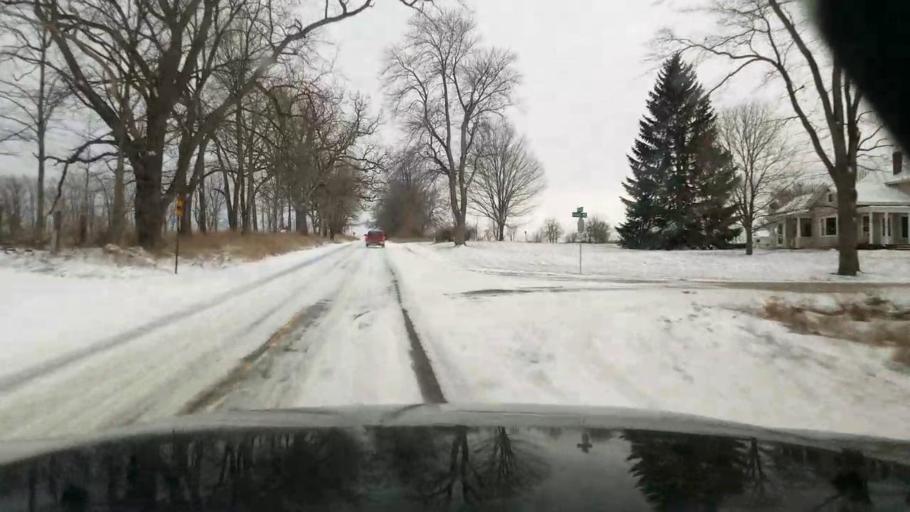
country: US
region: Michigan
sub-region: Jackson County
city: Spring Arbor
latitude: 42.1528
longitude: -84.4993
